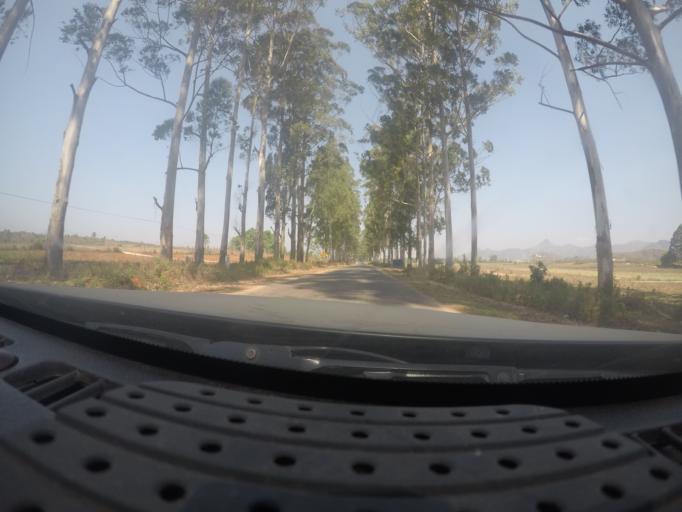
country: MM
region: Shan
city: Taunggyi
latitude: 20.8956
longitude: 96.5807
